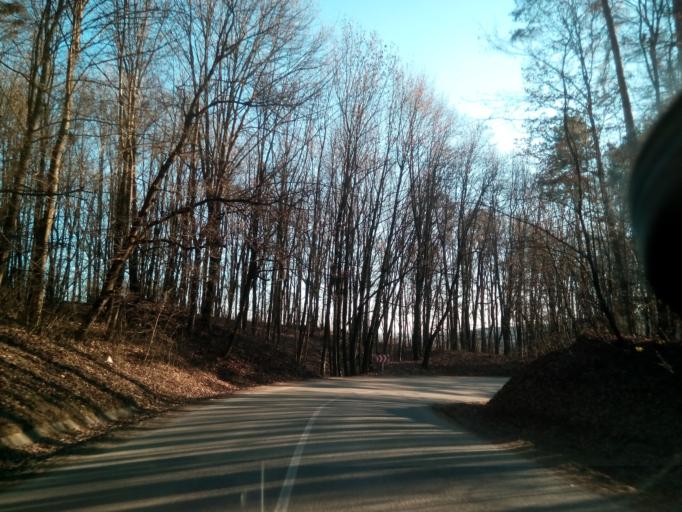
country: SK
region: Kosicky
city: Moldava nad Bodvou
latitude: 48.6829
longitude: 20.9795
